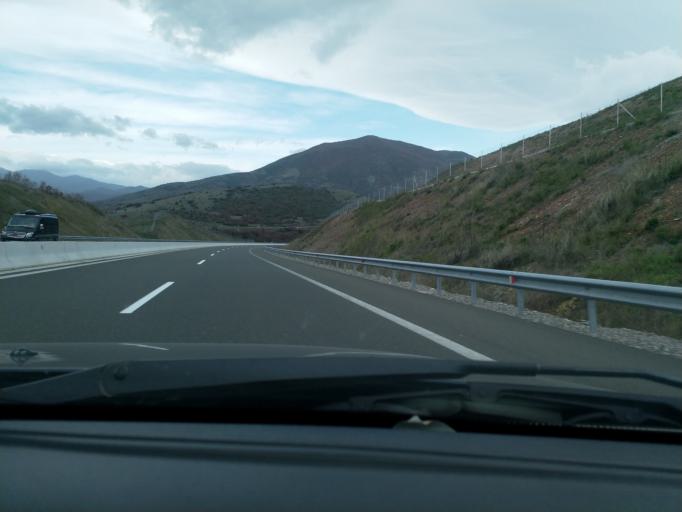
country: GR
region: Thessaly
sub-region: Nomos Kardhitsas
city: Anavra
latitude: 39.1551
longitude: 22.1084
